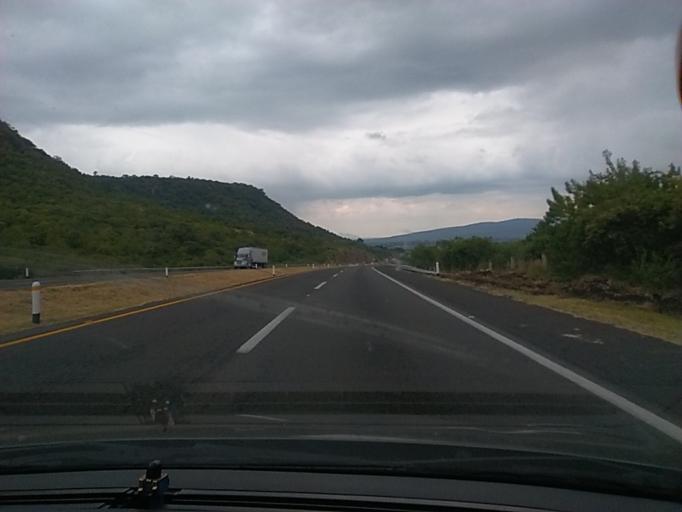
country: MX
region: Jalisco
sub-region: Zapotlan del Rey
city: Zapotlan del Rey
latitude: 20.4751
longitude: -102.9285
